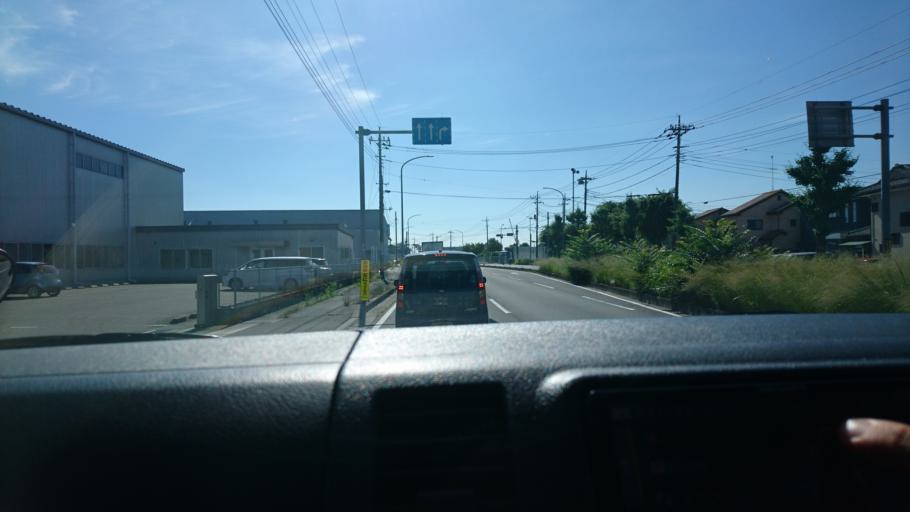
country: JP
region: Saitama
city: Kazo
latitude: 36.1264
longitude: 139.6362
